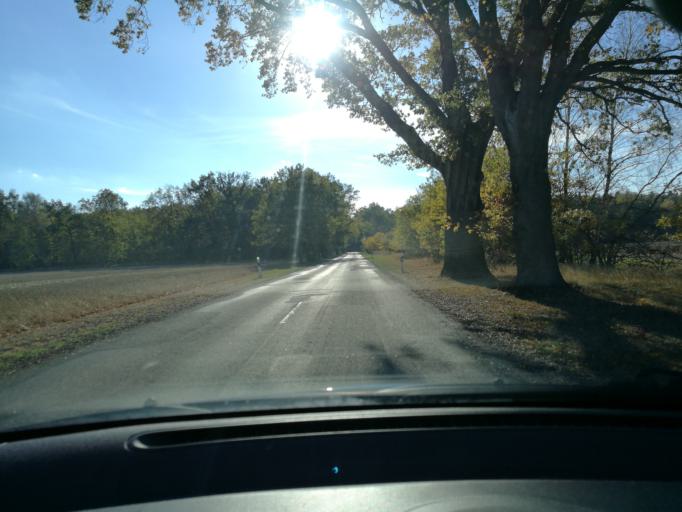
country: DE
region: Mecklenburg-Vorpommern
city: Neu Kaliss
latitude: 53.1317
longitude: 11.3182
